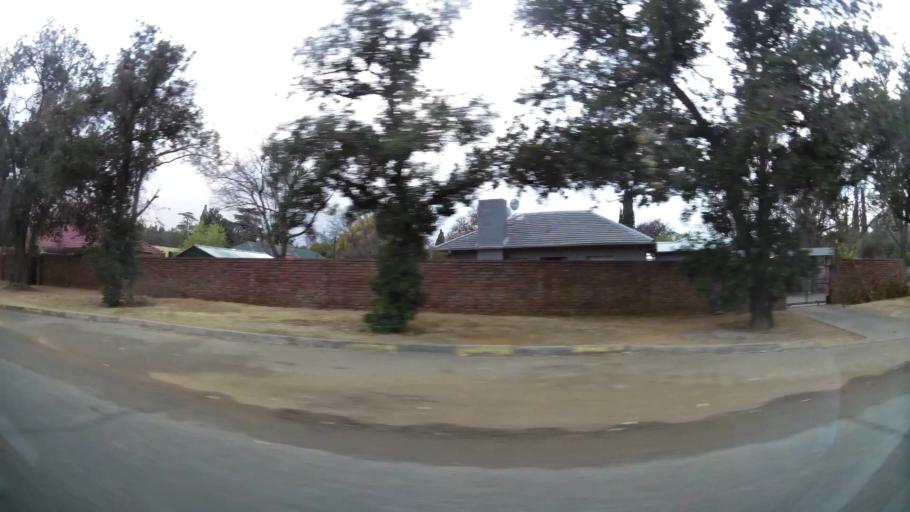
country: ZA
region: Orange Free State
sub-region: Lejweleputswa District Municipality
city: Welkom
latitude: -27.9597
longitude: 26.7375
